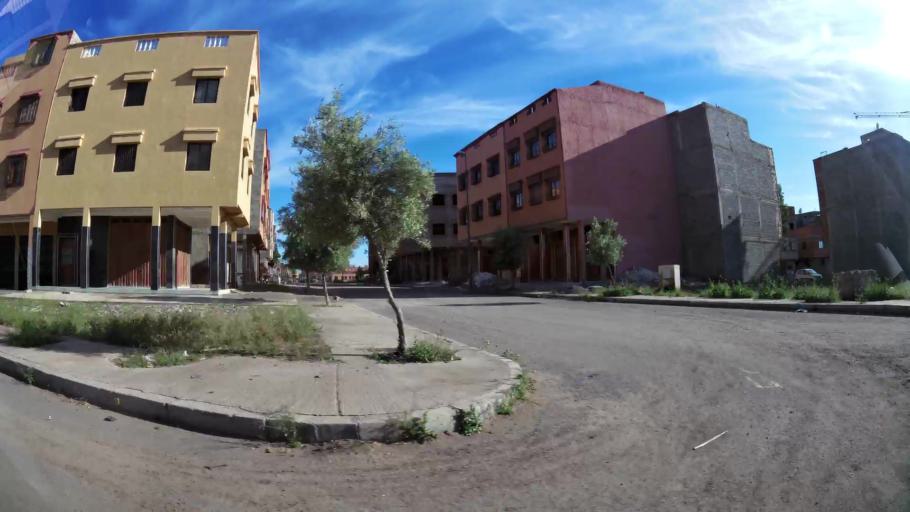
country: MA
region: Marrakech-Tensift-Al Haouz
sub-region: Marrakech
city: Marrakesh
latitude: 31.6901
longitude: -8.0665
